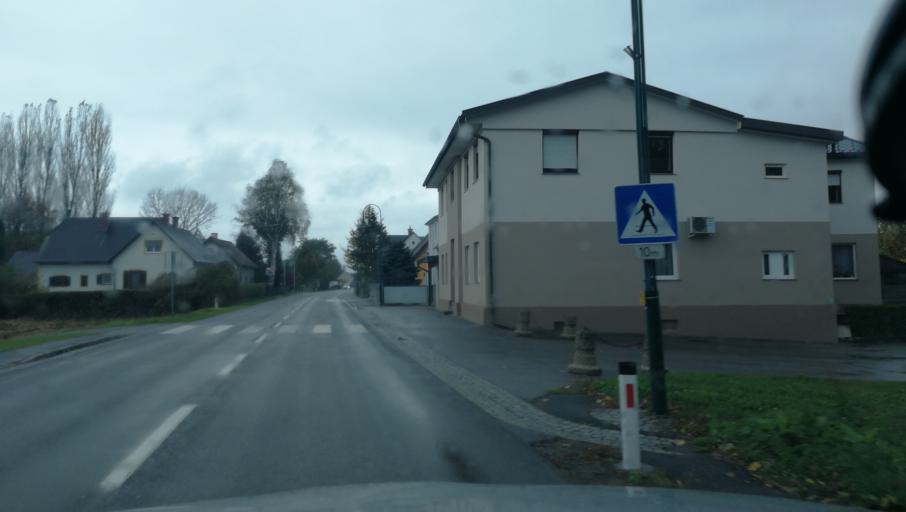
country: AT
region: Styria
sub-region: Politischer Bezirk Leibnitz
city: Strass in Steiermark
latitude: 46.7254
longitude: 15.6354
